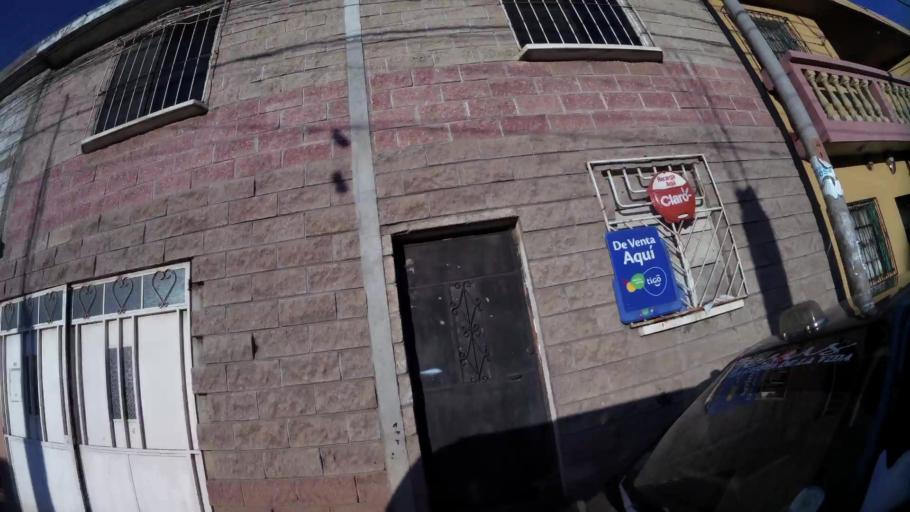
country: GT
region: Guatemala
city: Villa Nueva
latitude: 14.5175
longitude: -90.5818
